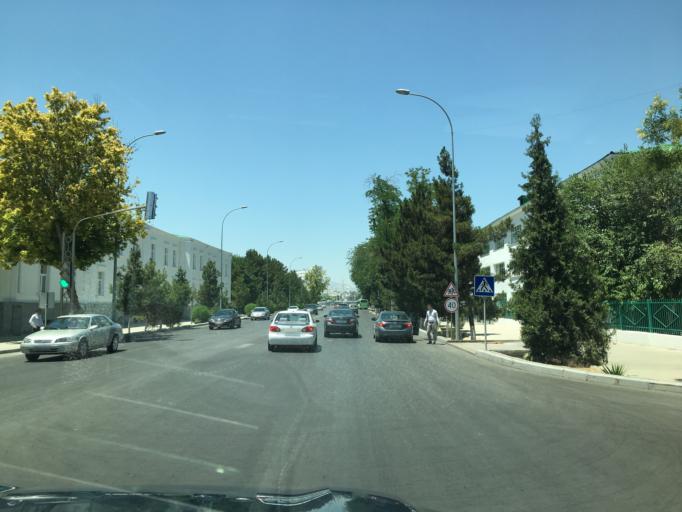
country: TM
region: Ahal
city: Ashgabat
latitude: 37.9417
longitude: 58.3713
